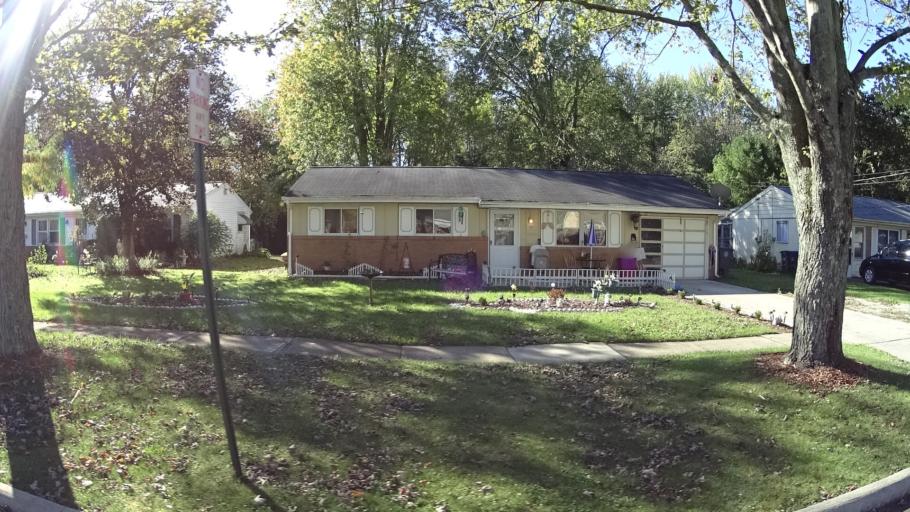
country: US
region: Ohio
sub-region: Lorain County
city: Oberlin
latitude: 41.2810
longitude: -82.2132
